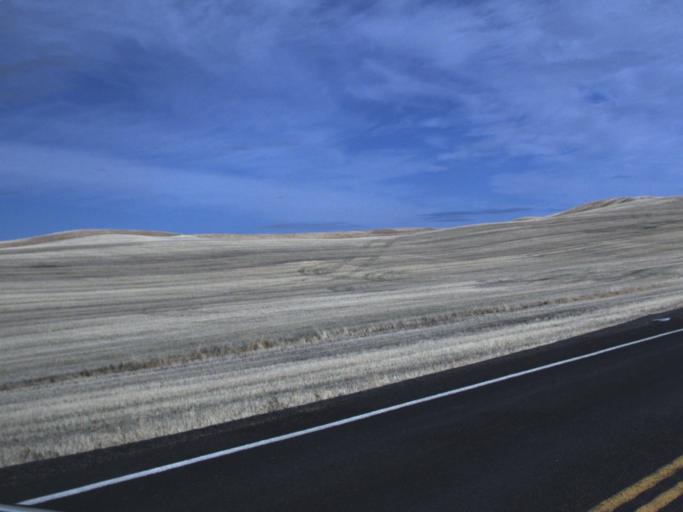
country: US
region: Idaho
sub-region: Latah County
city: Moscow
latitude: 46.9260
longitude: -117.0519
